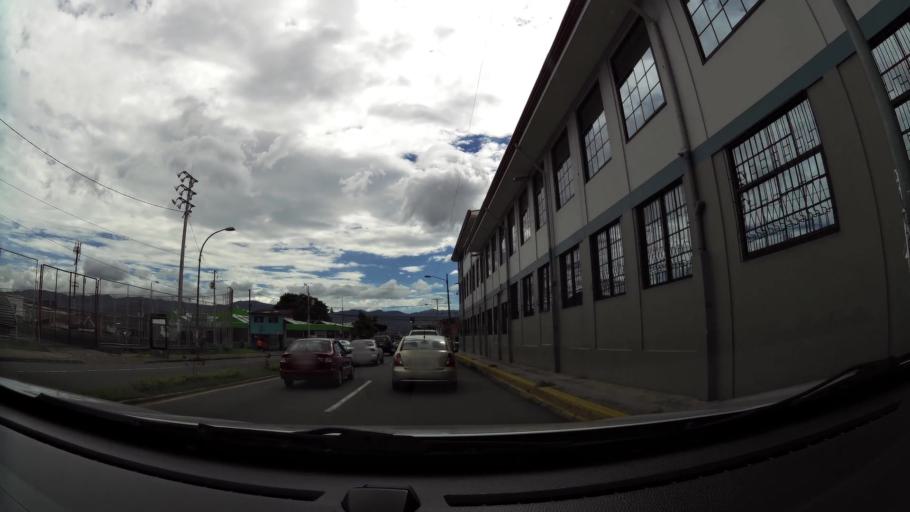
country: CR
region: San Jose
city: San Jose
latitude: 9.9242
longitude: -84.0749
